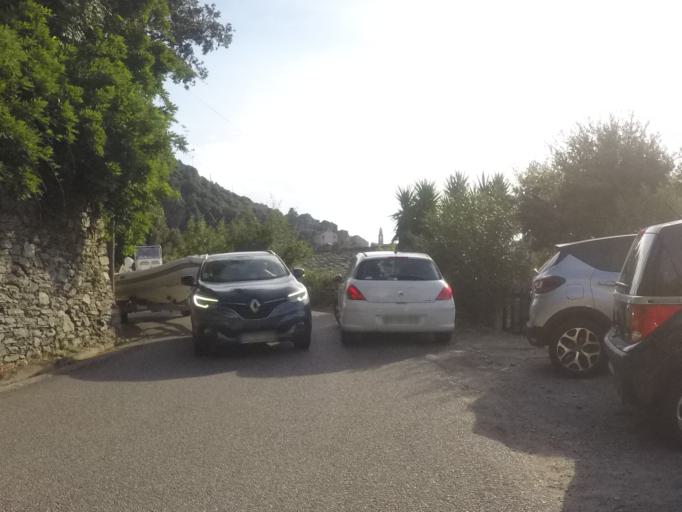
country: FR
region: Corsica
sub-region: Departement de la Haute-Corse
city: Santa-Maria-di-Lota
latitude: 42.7874
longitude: 9.3483
